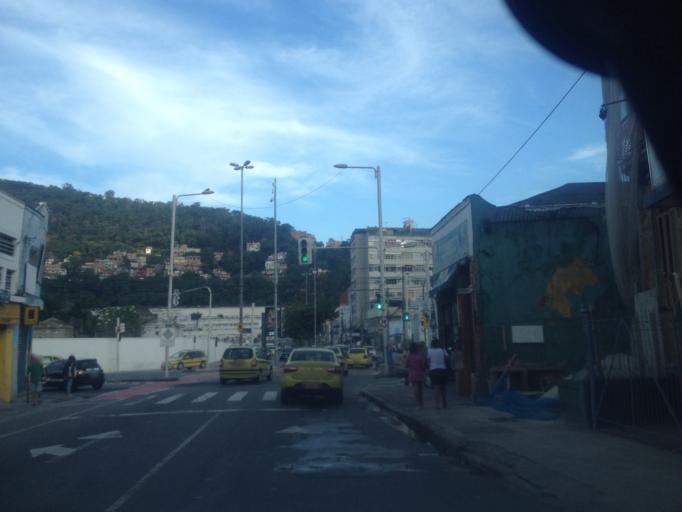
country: BR
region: Rio de Janeiro
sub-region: Rio De Janeiro
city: Rio de Janeiro
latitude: -22.9577
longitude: -43.1916
